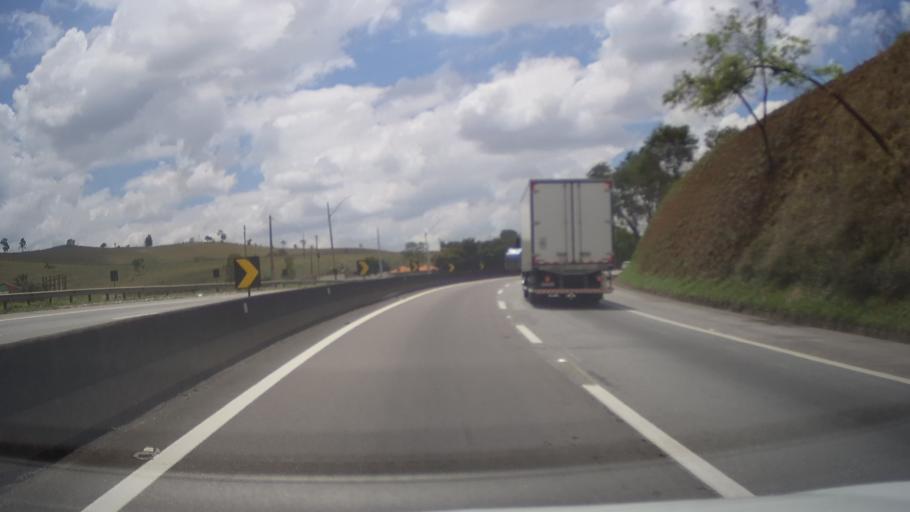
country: BR
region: Minas Gerais
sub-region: Tres Coracoes
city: Tres Coracoes
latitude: -21.6979
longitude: -45.3665
